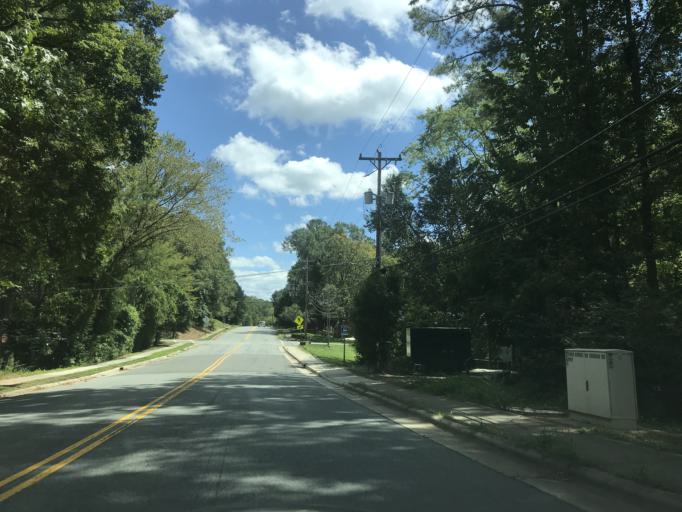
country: US
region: North Carolina
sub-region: Orange County
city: Chapel Hill
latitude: 35.9326
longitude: -79.0122
